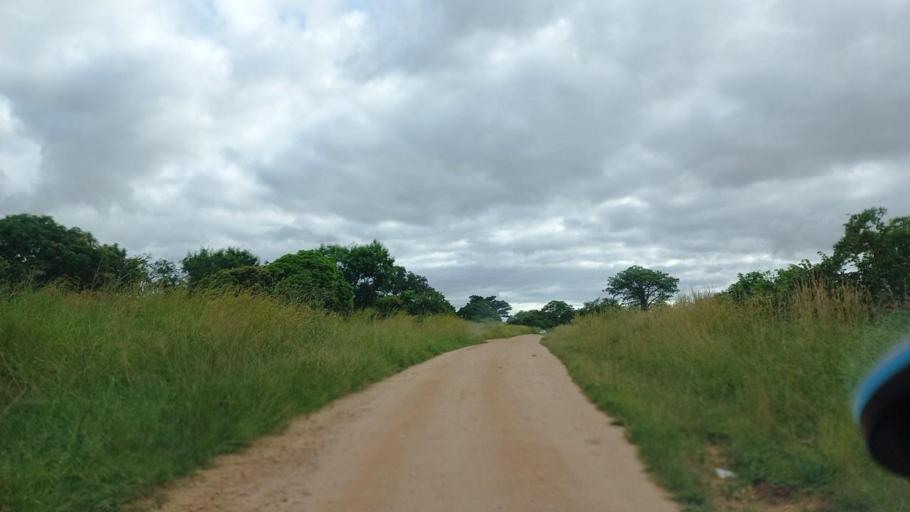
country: ZM
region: Lusaka
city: Chongwe
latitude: -15.4498
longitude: 28.8352
